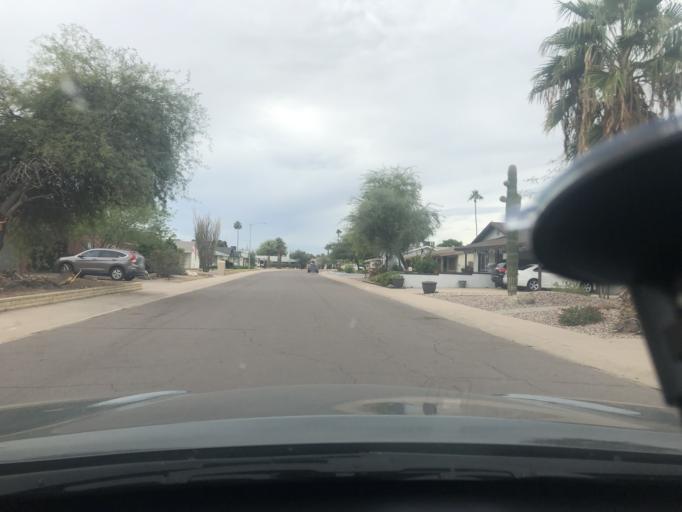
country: US
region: Arizona
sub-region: Maricopa County
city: Scottsdale
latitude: 33.4916
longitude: -111.8966
